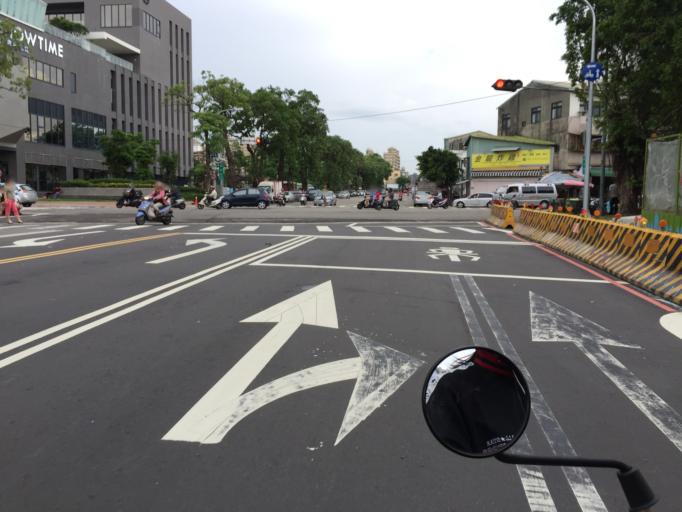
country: TW
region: Taiwan
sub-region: Taichung City
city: Taichung
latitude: 24.1398
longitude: 120.6924
